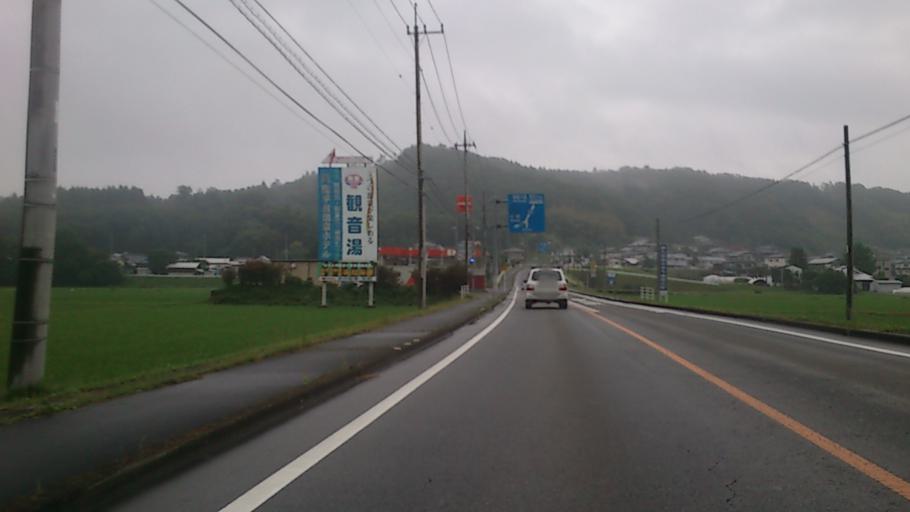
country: JP
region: Tochigi
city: Karasuyama
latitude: 36.7493
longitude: 140.1438
